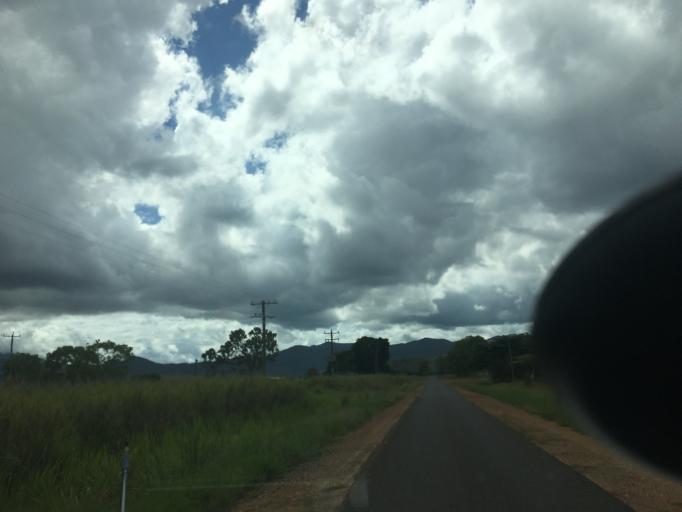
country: AU
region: Queensland
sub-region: Tablelands
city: Mareeba
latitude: -16.9961
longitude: 145.5229
